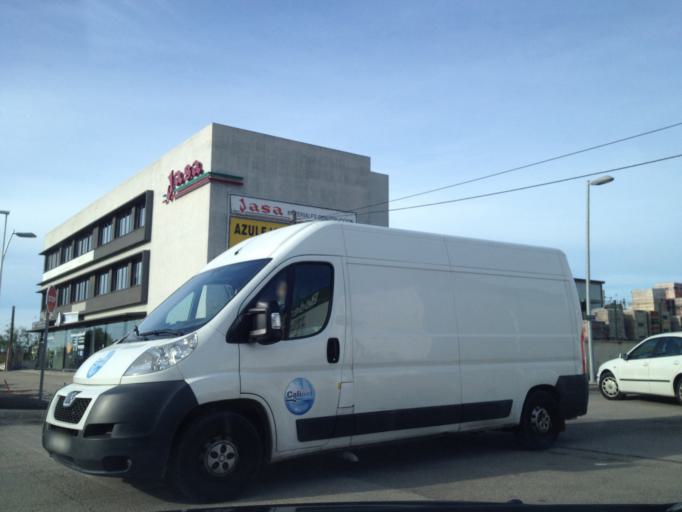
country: ES
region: Balearic Islands
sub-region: Illes Balears
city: Marratxi
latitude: 39.6208
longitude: 2.7243
